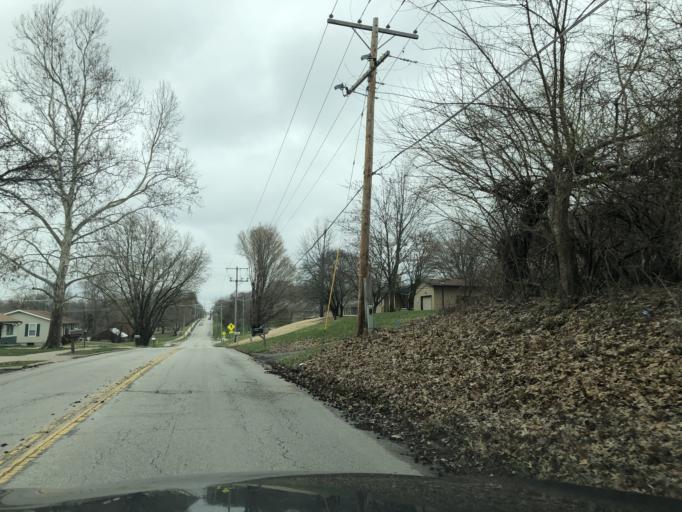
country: US
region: Kansas
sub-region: Leavenworth County
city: Lansing
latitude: 39.2755
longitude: -94.9184
